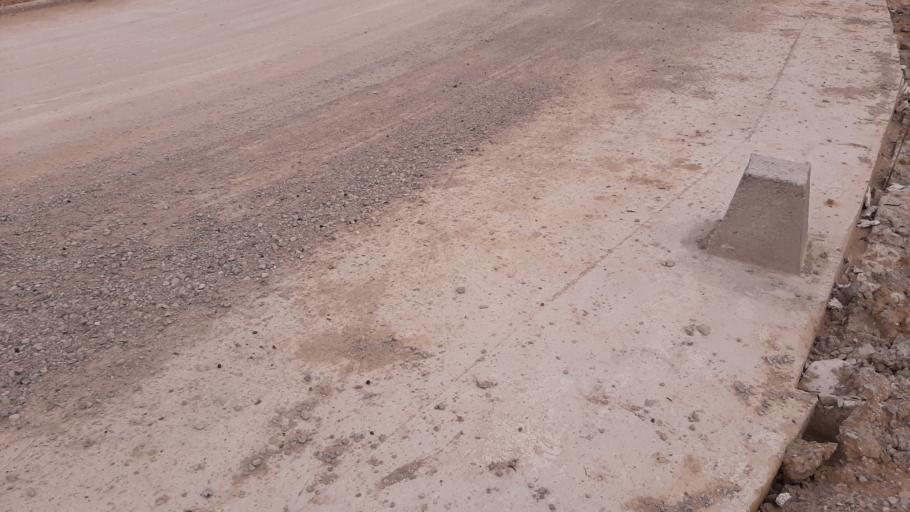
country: TN
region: Al Munastir
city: Jammal
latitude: 35.6500
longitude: 10.7804
